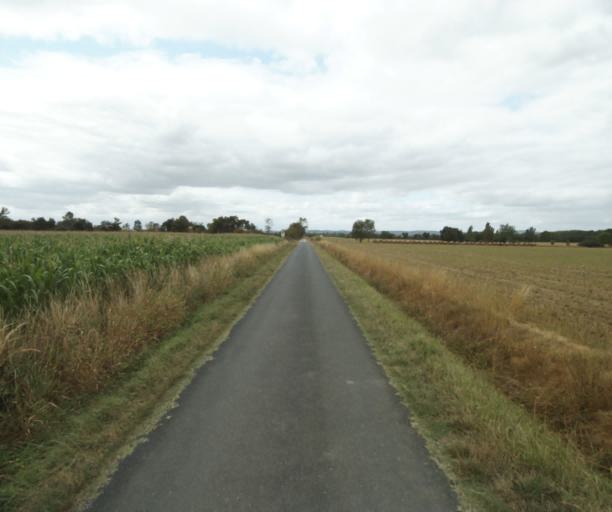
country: FR
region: Midi-Pyrenees
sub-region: Departement de la Haute-Garonne
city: Revel
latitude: 43.4755
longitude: 2.0344
